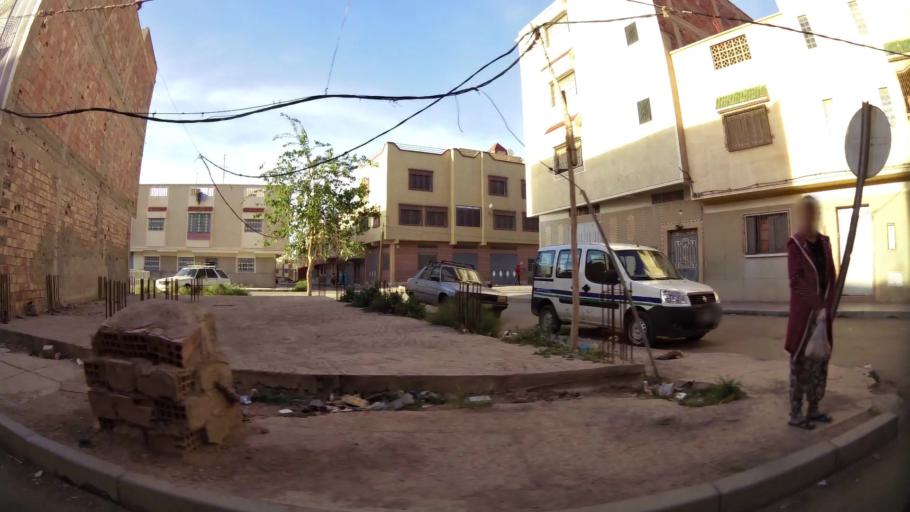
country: MA
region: Oriental
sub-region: Oujda-Angad
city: Oujda
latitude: 34.6759
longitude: -1.9017
